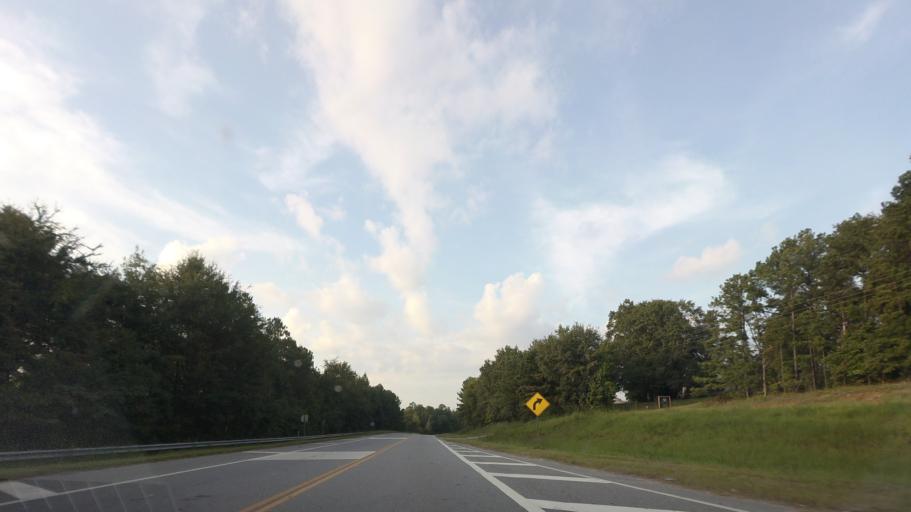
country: US
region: Georgia
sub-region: Wilkinson County
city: Gordon
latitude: 32.8614
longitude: -83.3470
